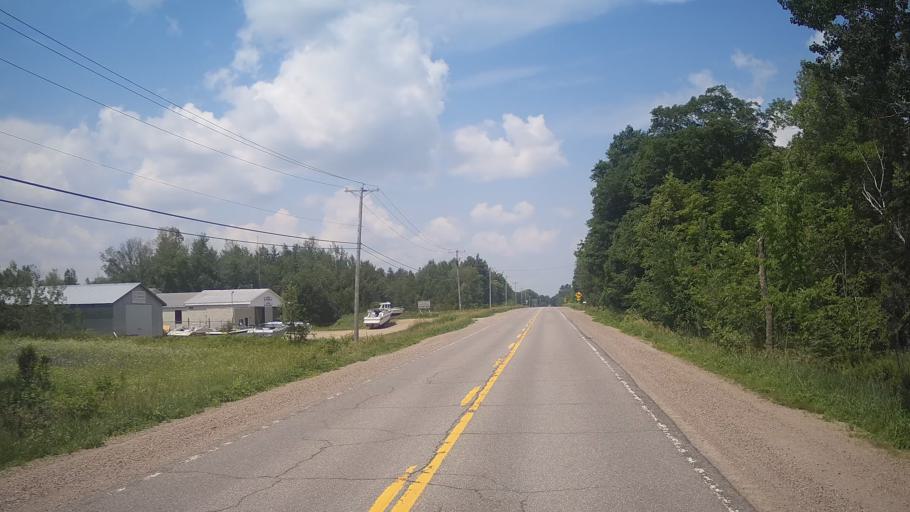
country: CA
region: Quebec
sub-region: Outaouais
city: Shawville
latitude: 45.5706
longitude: -76.4360
